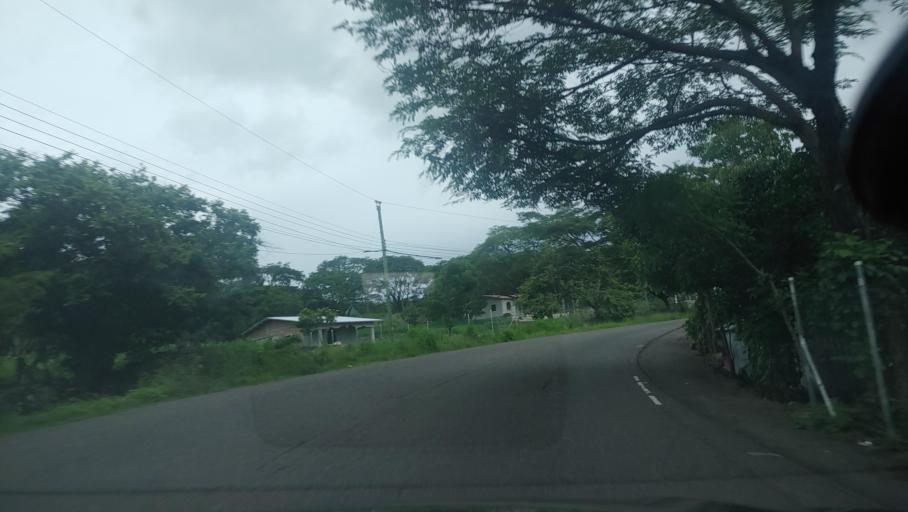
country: HN
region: Choluteca
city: Corpus
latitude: 13.3702
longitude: -86.9968
